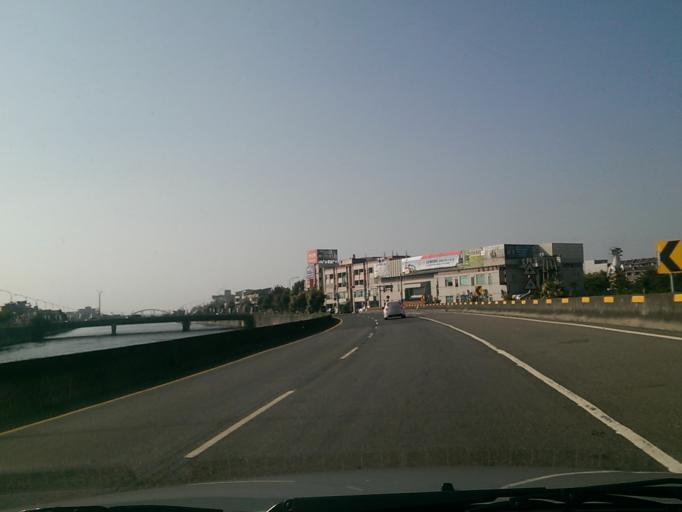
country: TW
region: Taiwan
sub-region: Changhua
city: Chang-hua
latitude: 24.0453
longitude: 120.4388
